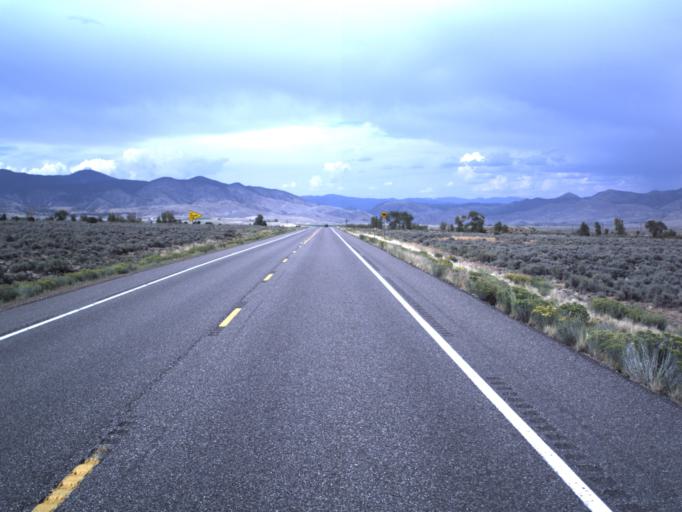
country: US
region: Utah
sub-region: Piute County
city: Junction
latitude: 38.3794
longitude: -112.2277
